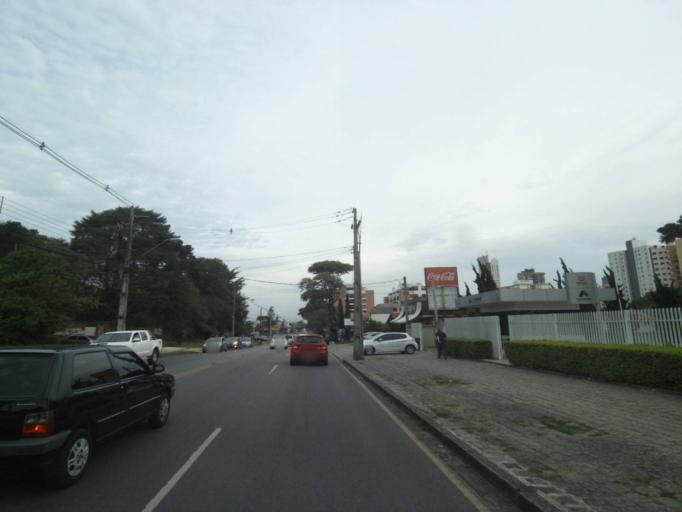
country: BR
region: Parana
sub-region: Curitiba
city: Curitiba
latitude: -25.4341
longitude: -49.2370
